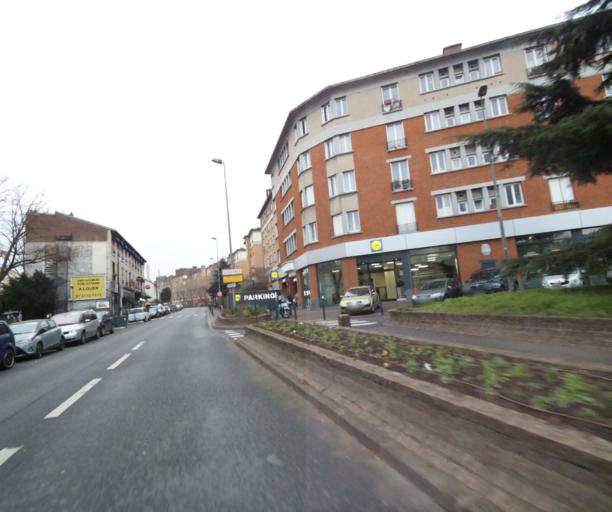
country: FR
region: Ile-de-France
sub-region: Departement des Hauts-de-Seine
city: Rueil-Malmaison
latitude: 48.8661
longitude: 2.2022
